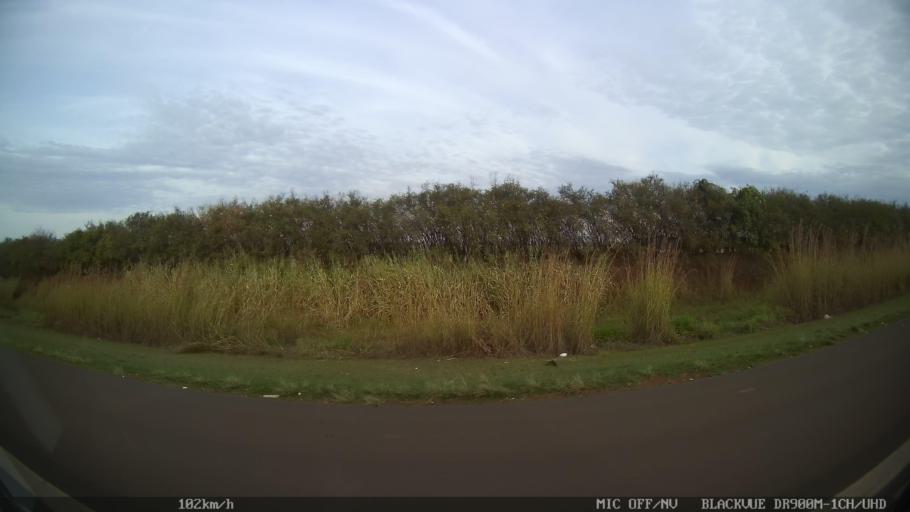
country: BR
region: Sao Paulo
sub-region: Iracemapolis
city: Iracemapolis
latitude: -22.6676
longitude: -47.5376
